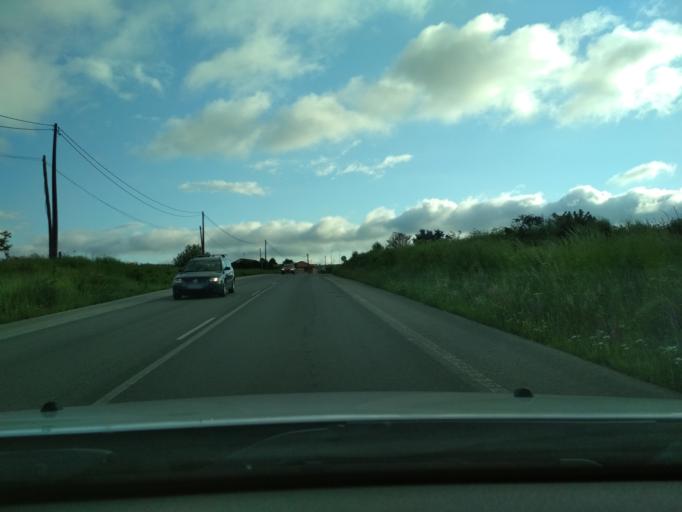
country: ES
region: Galicia
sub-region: Provincia da Coruna
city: Mazaricos
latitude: 42.9652
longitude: -8.9100
